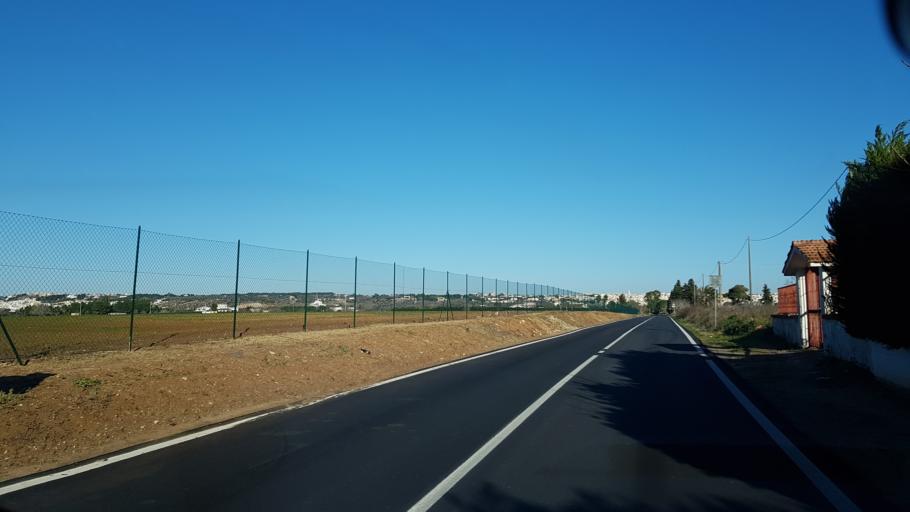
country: IT
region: Apulia
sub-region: Provincia di Lecce
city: Melissano
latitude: 39.9998
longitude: 18.1332
